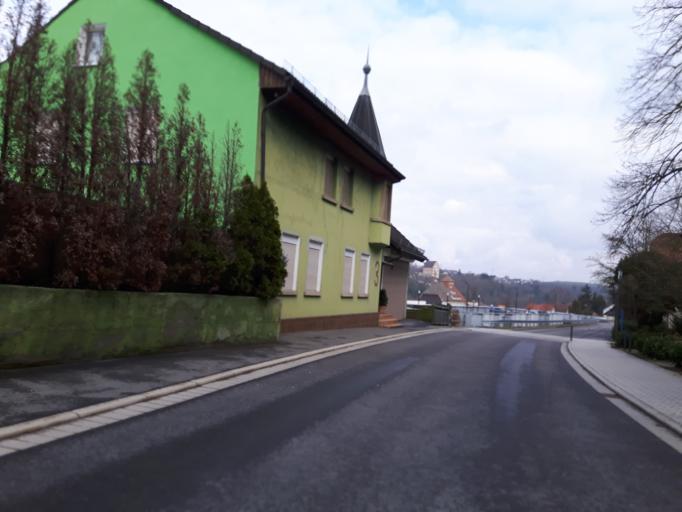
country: DE
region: Baden-Wuerttemberg
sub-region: Regierungsbezirk Stuttgart
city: Neuenstadt am Kocher
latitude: 49.2377
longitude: 9.3302
